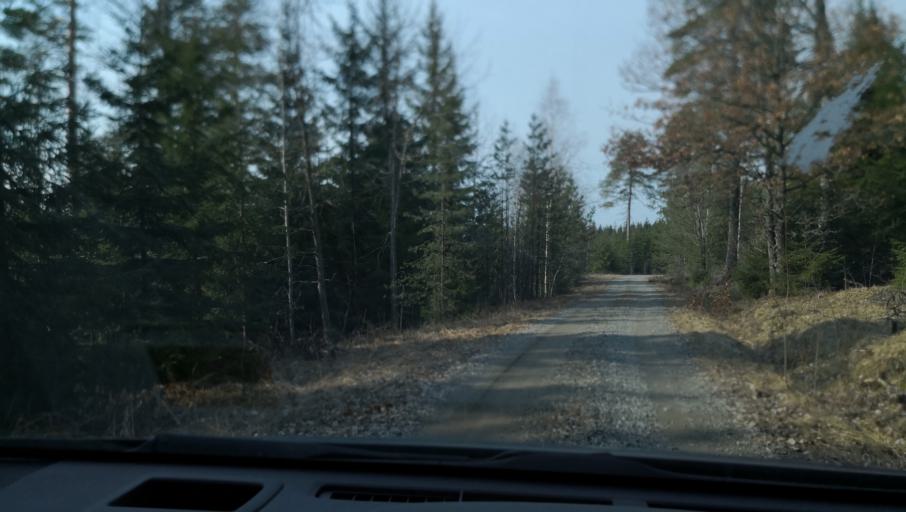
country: SE
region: OErebro
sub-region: Lindesbergs Kommun
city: Frovi
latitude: 59.3827
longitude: 15.4117
